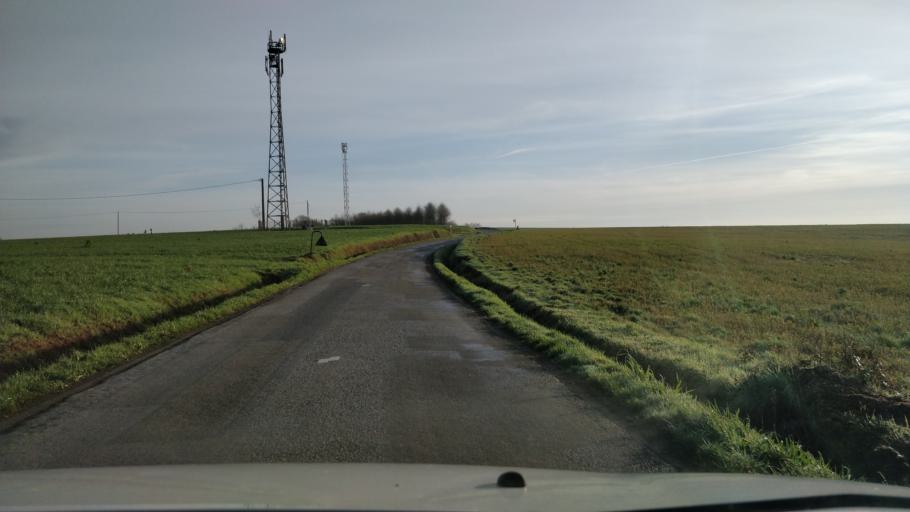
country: FR
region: Brittany
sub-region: Departement d'Ille-et-Vilaine
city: Bais
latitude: 48.0097
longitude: -1.3046
